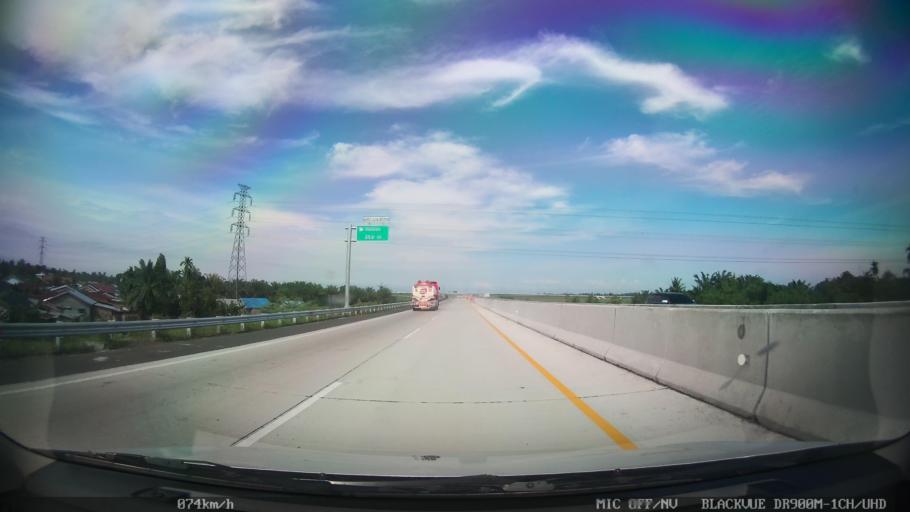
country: ID
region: North Sumatra
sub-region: Kabupaten Langkat
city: Stabat
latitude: 3.7133
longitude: 98.5029
